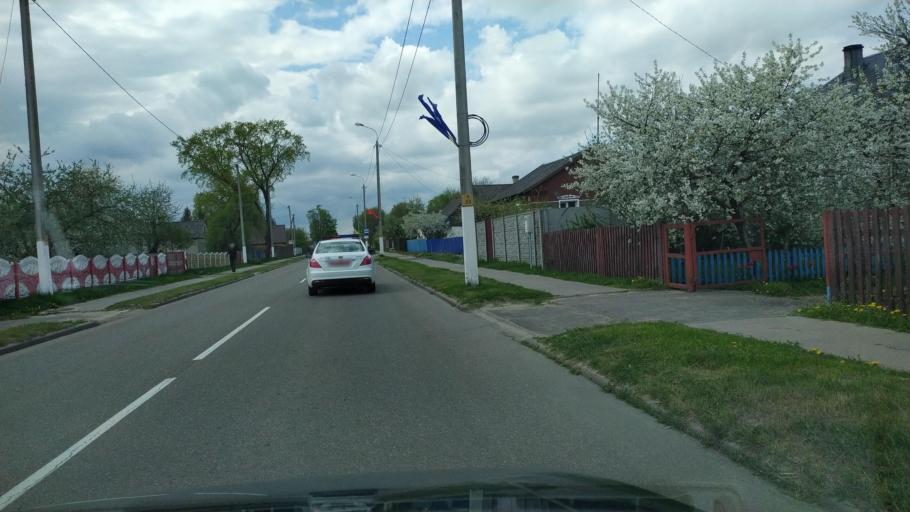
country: BY
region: Brest
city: Pruzhany
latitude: 52.5572
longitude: 24.4344
